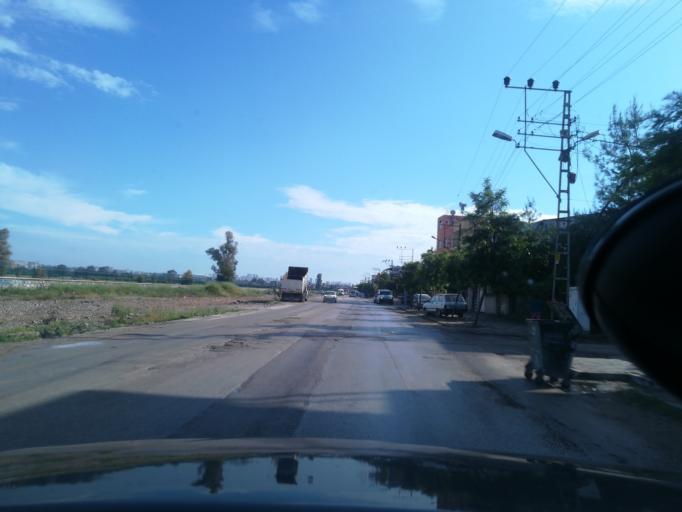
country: TR
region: Adana
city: Adana
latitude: 37.0122
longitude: 35.3592
